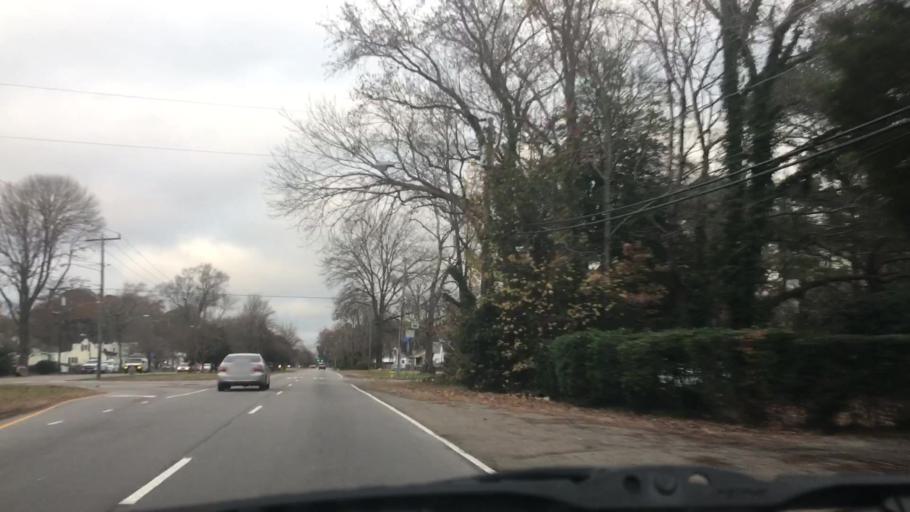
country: US
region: Virginia
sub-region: City of Norfolk
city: Norfolk
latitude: 36.9174
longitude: -76.2418
